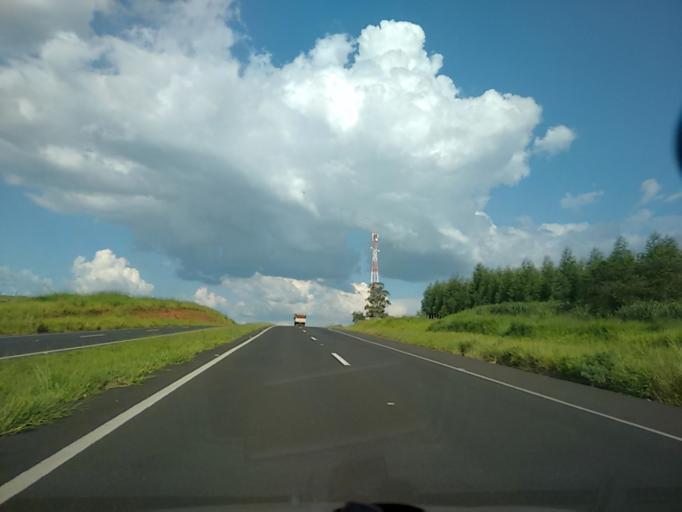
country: BR
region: Sao Paulo
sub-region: Duartina
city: Duartina
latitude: -22.3248
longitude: -49.4218
